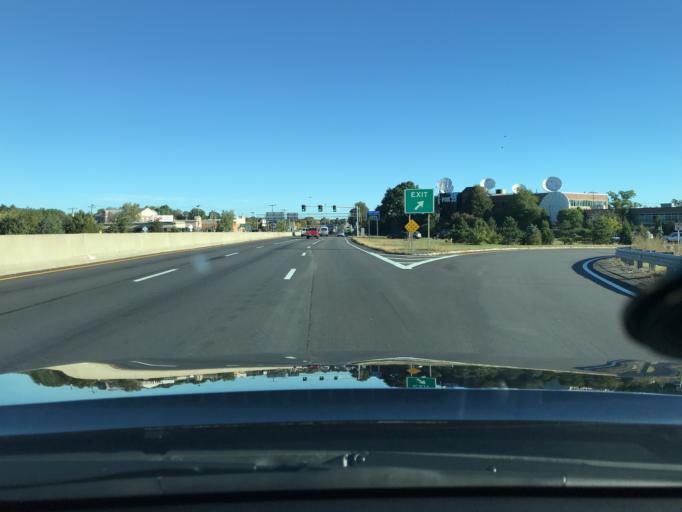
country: US
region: Massachusetts
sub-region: Norfolk County
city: Dedham
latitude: 42.2290
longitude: -71.1815
